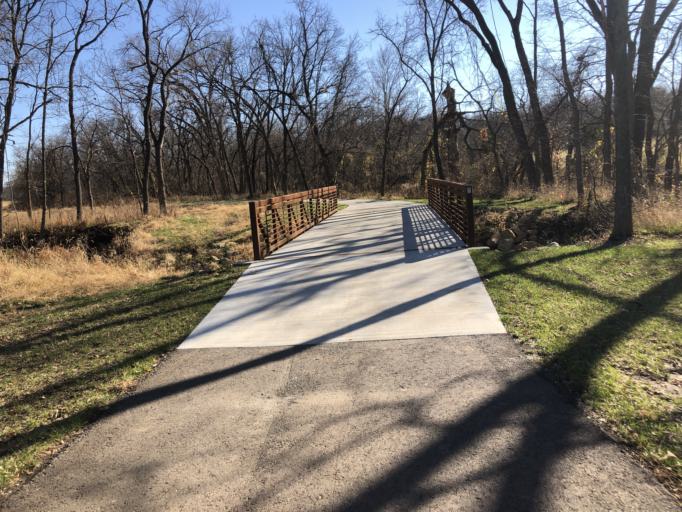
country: US
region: Kansas
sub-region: Johnson County
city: Gardner
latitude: 38.8794
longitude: -94.9671
